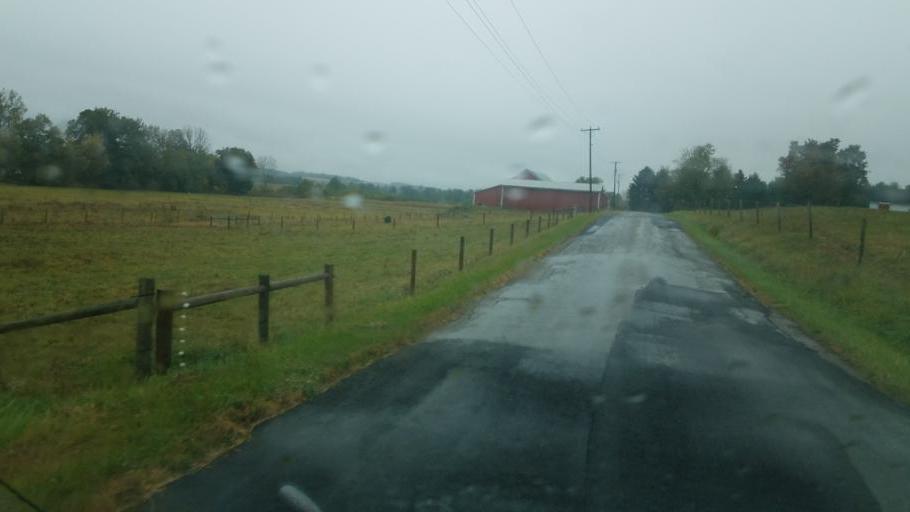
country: US
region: Ohio
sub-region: Knox County
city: Danville
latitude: 40.4919
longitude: -82.2880
